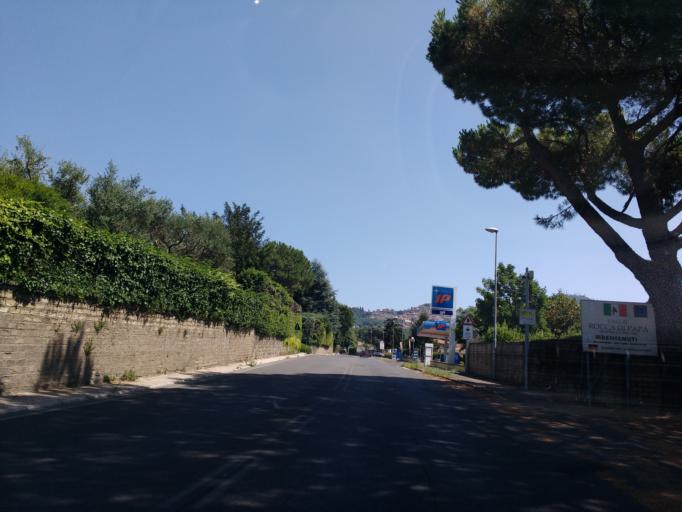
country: IT
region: Latium
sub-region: Citta metropolitana di Roma Capitale
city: Rocca di Papa
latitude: 41.7760
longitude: 12.6892
